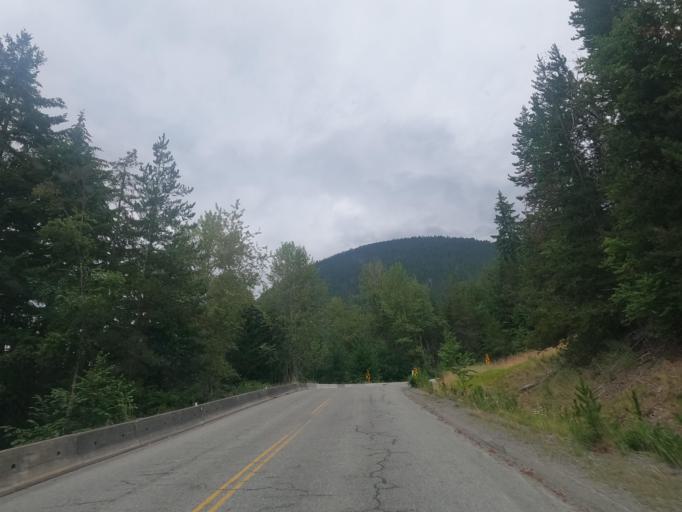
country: CA
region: British Columbia
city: Pemberton
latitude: 50.3029
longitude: -122.5853
